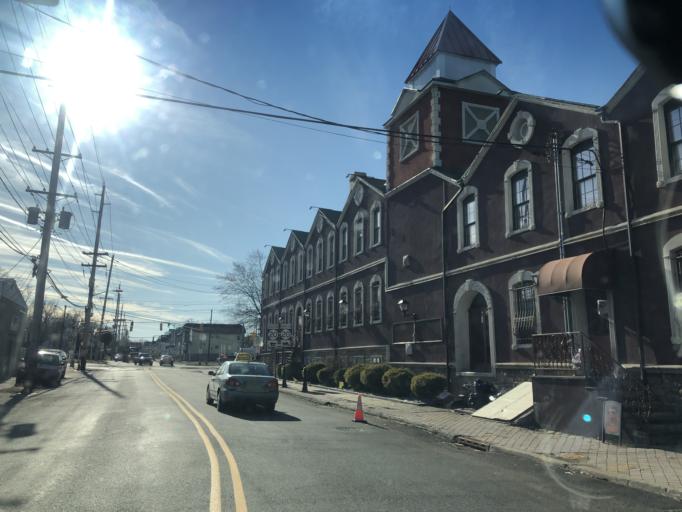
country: US
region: New Jersey
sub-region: Bergen County
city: Fair Lawn
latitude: 40.9239
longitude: -74.1409
